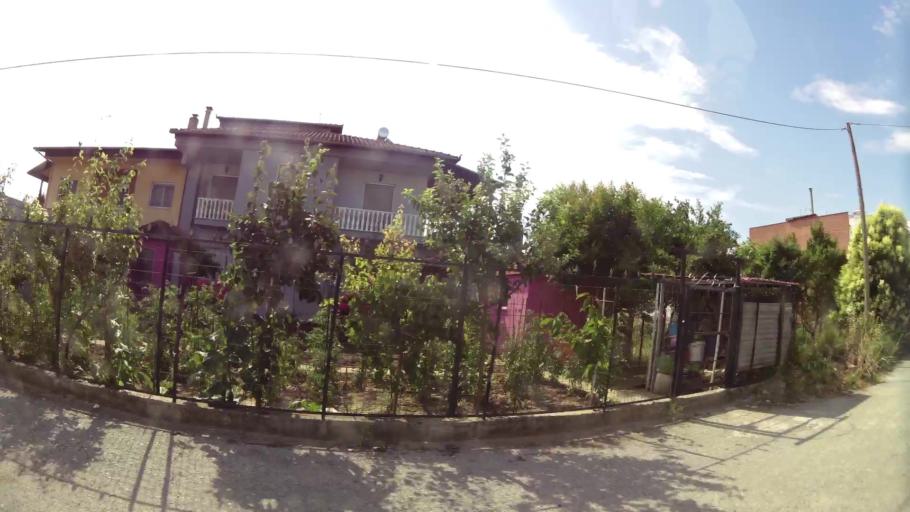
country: GR
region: Central Macedonia
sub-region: Nomos Pierias
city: Katerini
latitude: 40.2826
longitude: 22.5077
